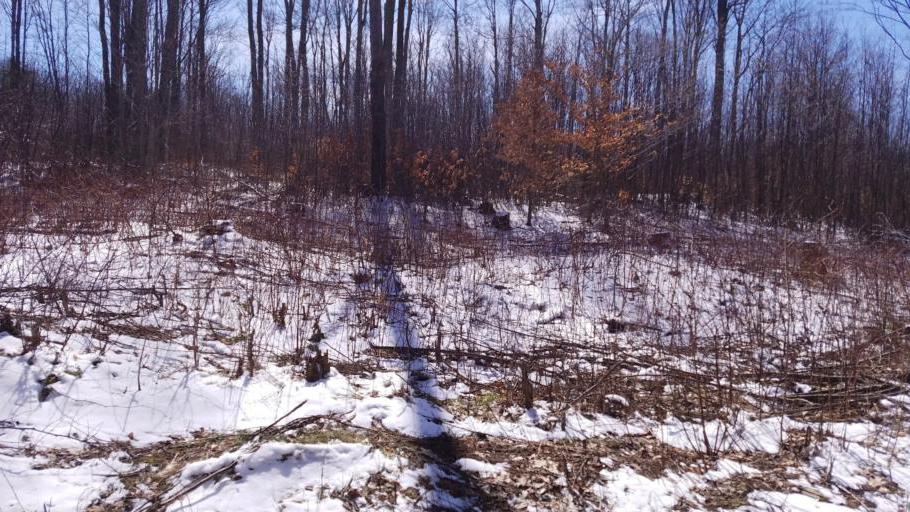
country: US
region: Pennsylvania
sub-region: Tioga County
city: Westfield
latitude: 41.9596
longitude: -77.7290
